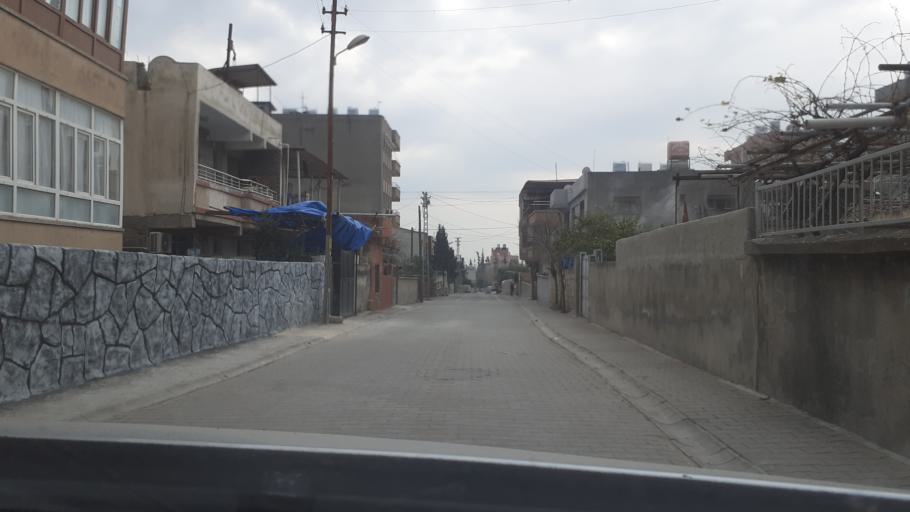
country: TR
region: Hatay
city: Kirikhan
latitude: 36.4941
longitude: 36.3525
